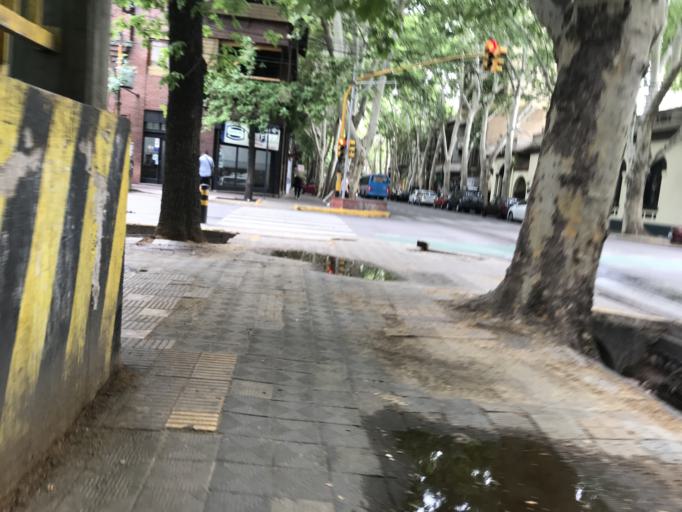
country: AR
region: Mendoza
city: Mendoza
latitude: -32.8866
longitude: -68.8451
